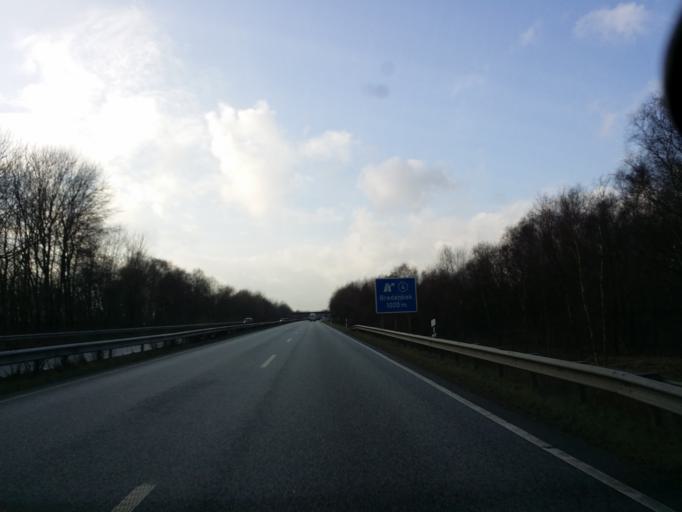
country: DE
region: Schleswig-Holstein
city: Bredenbek
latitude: 54.3148
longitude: 9.8767
